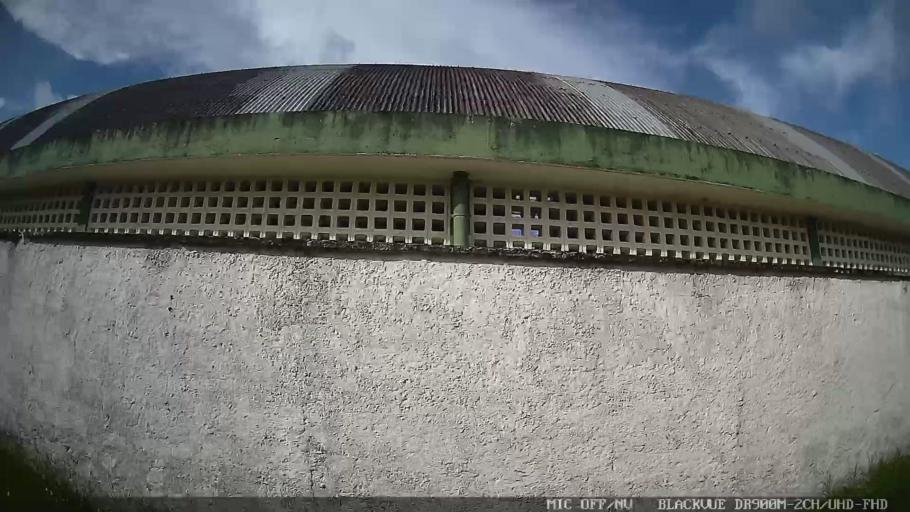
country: BR
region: Sao Paulo
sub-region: Itanhaem
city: Itanhaem
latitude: -24.1911
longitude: -46.8242
